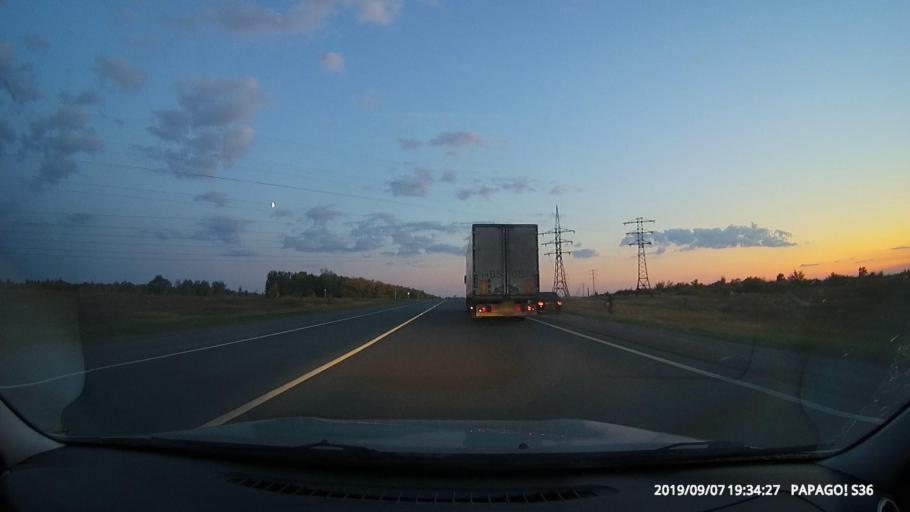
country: RU
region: Samara
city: Chapayevsk
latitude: 52.9973
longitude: 49.7728
